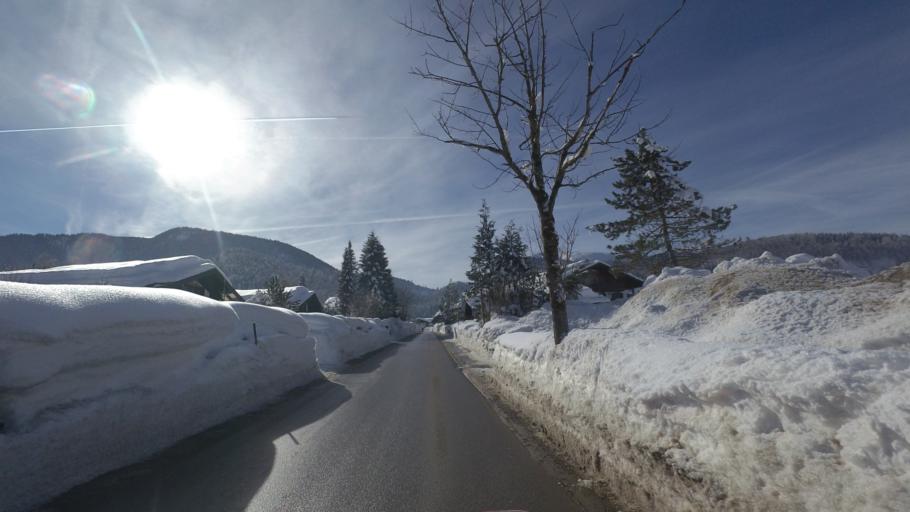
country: DE
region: Bavaria
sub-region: Upper Bavaria
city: Reit im Winkl
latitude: 47.6646
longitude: 12.4770
